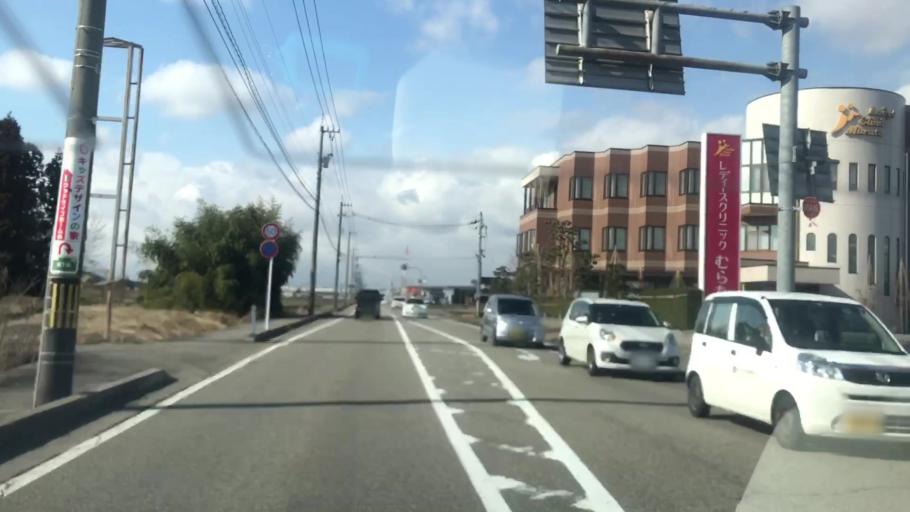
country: JP
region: Toyama
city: Nishishinminato
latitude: 36.7176
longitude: 137.0812
